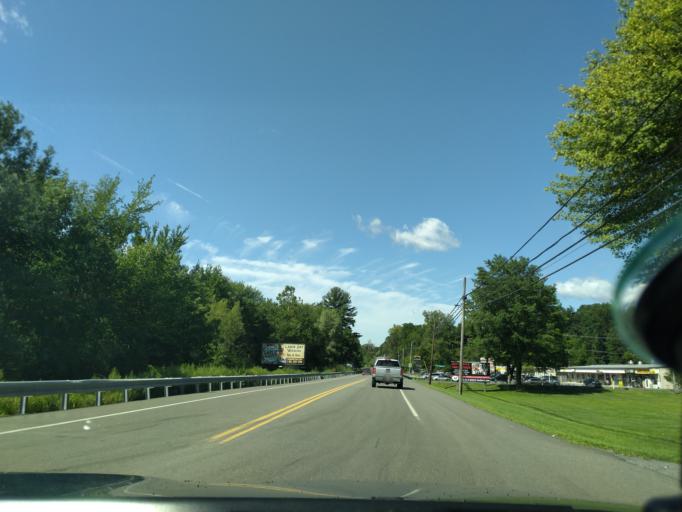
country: US
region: Pennsylvania
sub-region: Pike County
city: Saw Creek
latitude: 41.0690
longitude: -75.0437
